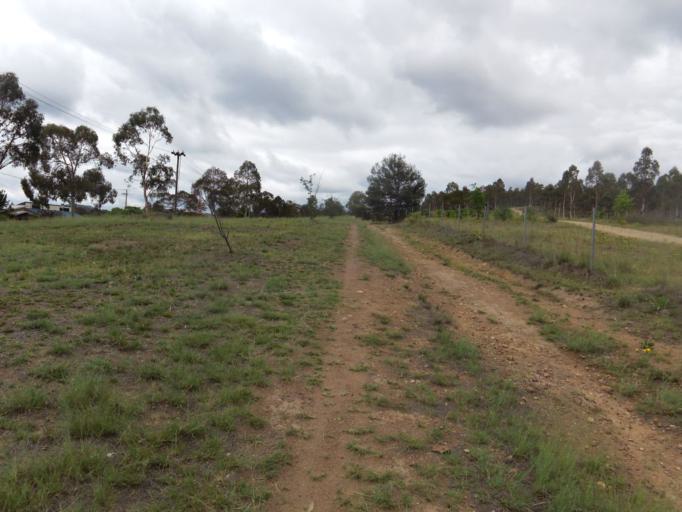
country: AU
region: Australian Capital Territory
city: Macquarie
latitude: -35.3327
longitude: 149.0266
